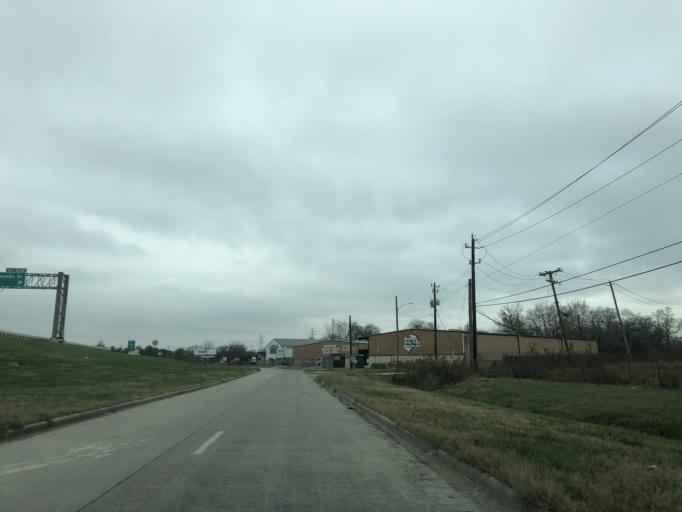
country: US
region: Texas
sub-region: Harris County
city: Jacinto City
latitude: 29.8035
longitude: -95.2805
